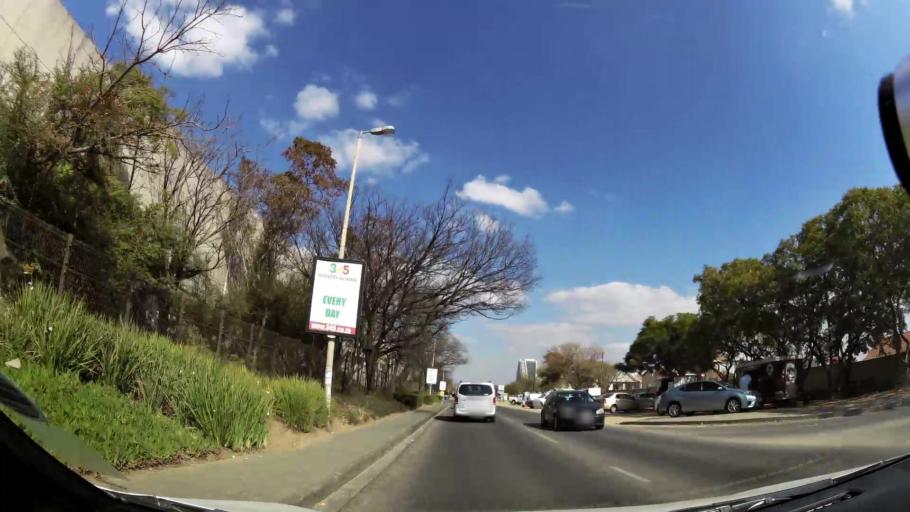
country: ZA
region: Gauteng
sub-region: City of Johannesburg Metropolitan Municipality
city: Midrand
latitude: -26.0082
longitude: 28.1154
